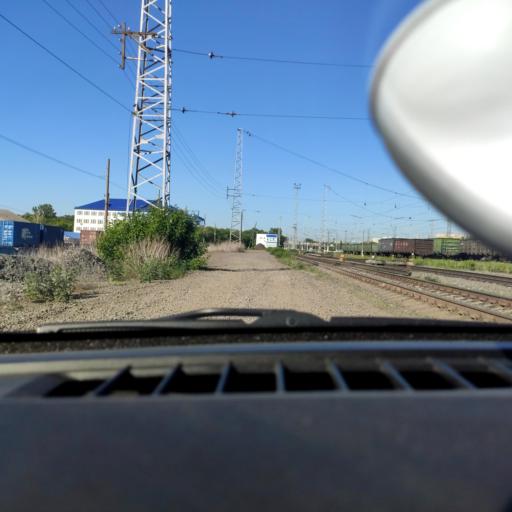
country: RU
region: Samara
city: Samara
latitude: 53.2053
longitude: 50.2517
